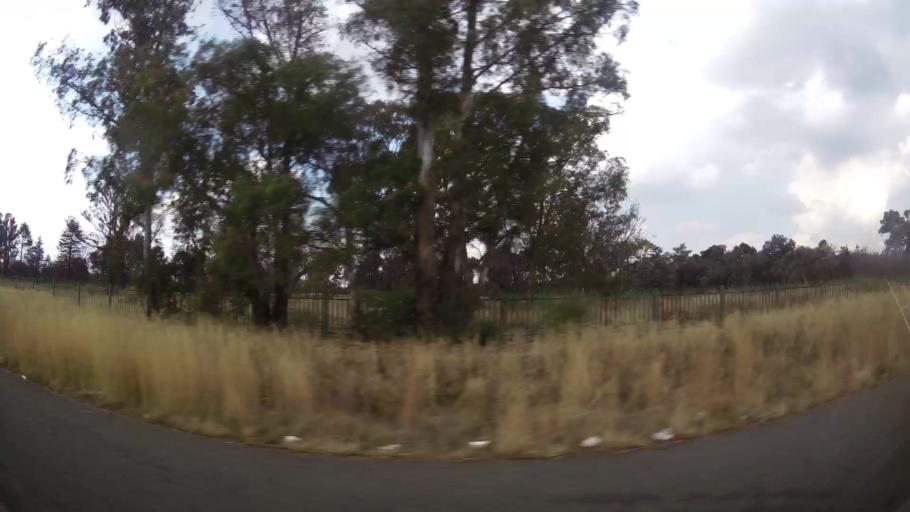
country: ZA
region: Gauteng
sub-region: Sedibeng District Municipality
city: Vereeniging
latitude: -26.6871
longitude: 27.9402
